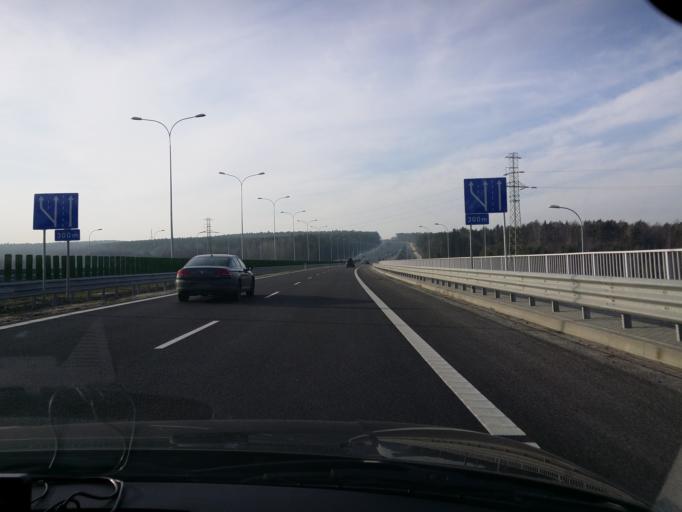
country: PL
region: Swietokrzyskie
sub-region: Powiat skarzyski
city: Skarzysko-Kamienna
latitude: 51.1584
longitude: 20.8520
